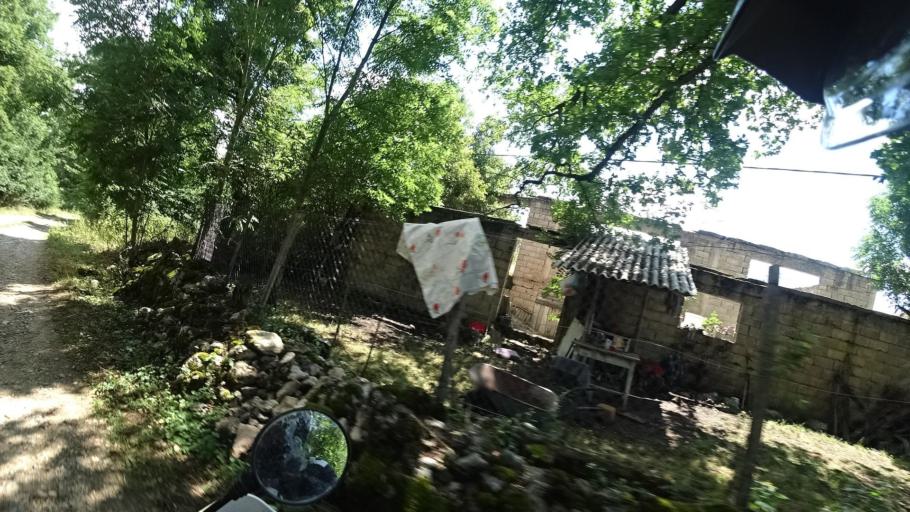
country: HR
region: Licko-Senjska
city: Gospic
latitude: 44.6191
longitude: 15.6258
